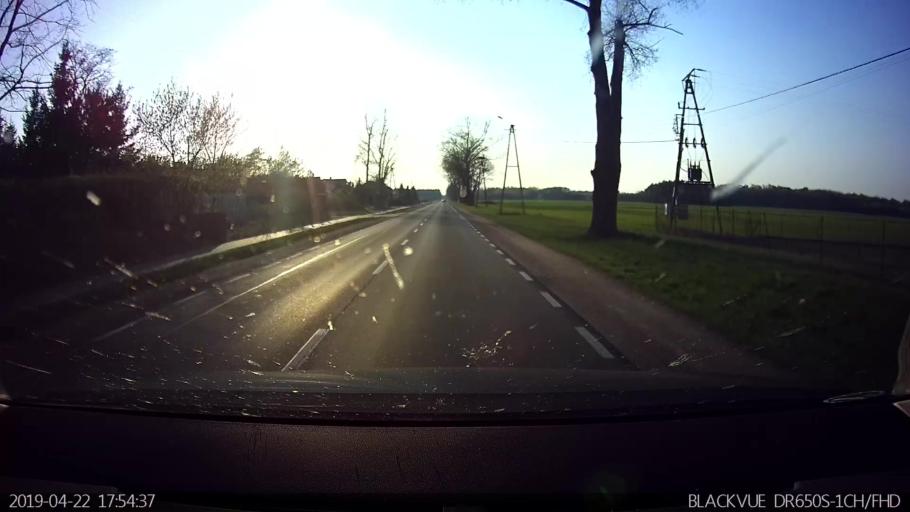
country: PL
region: Masovian Voivodeship
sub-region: Powiat wegrowski
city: Liw
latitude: 52.4580
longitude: 21.9356
